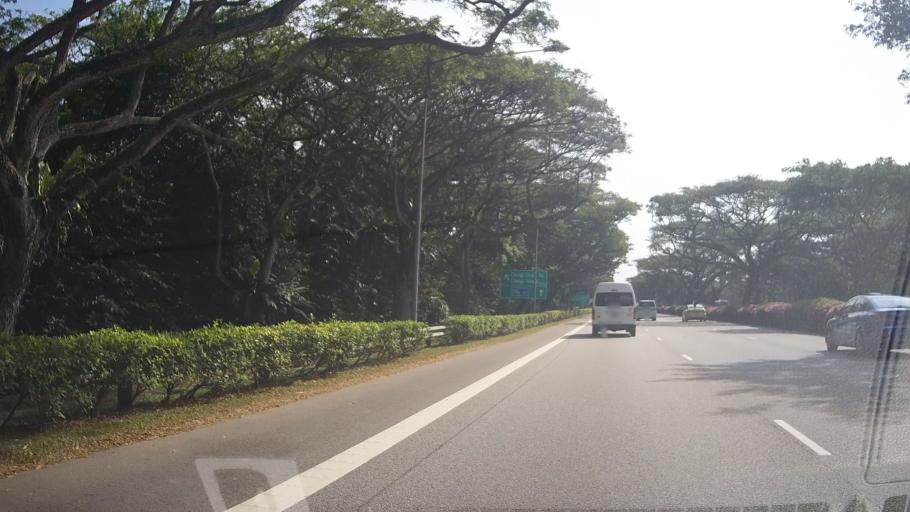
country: SG
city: Singapore
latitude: 1.3326
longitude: 103.9773
